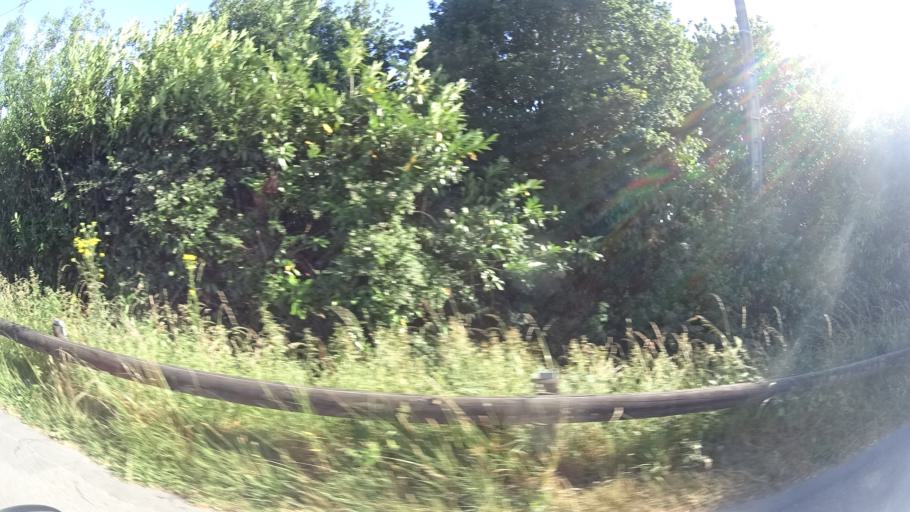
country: FR
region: Brittany
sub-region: Departement d'Ille-et-Vilaine
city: Langon
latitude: 47.7392
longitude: -1.8443
